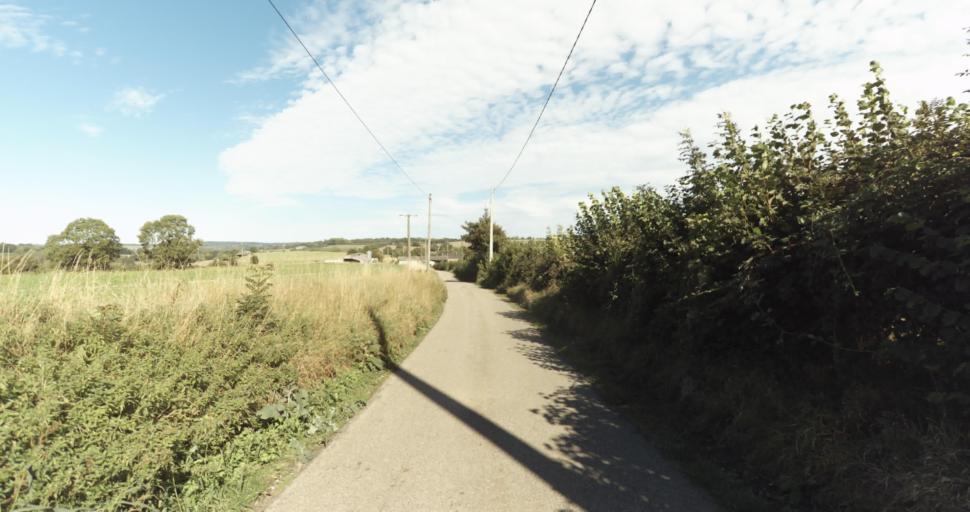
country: FR
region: Lower Normandy
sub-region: Departement de l'Orne
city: Gace
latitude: 48.8029
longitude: 0.2298
